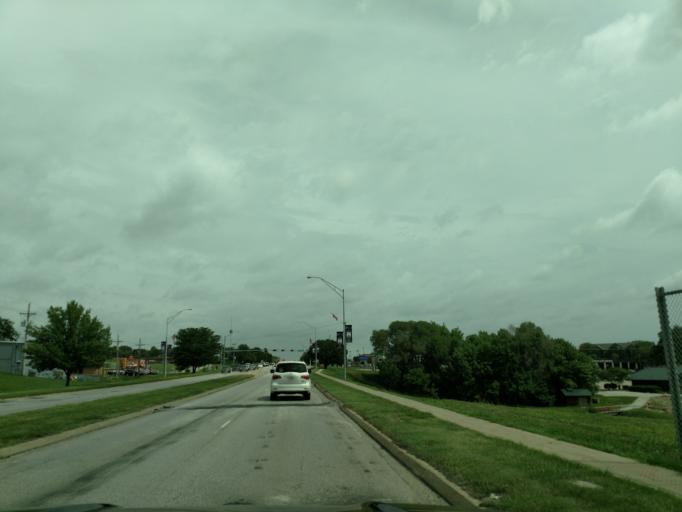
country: US
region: Nebraska
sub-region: Sarpy County
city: La Vista
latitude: 41.1858
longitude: -96.0429
